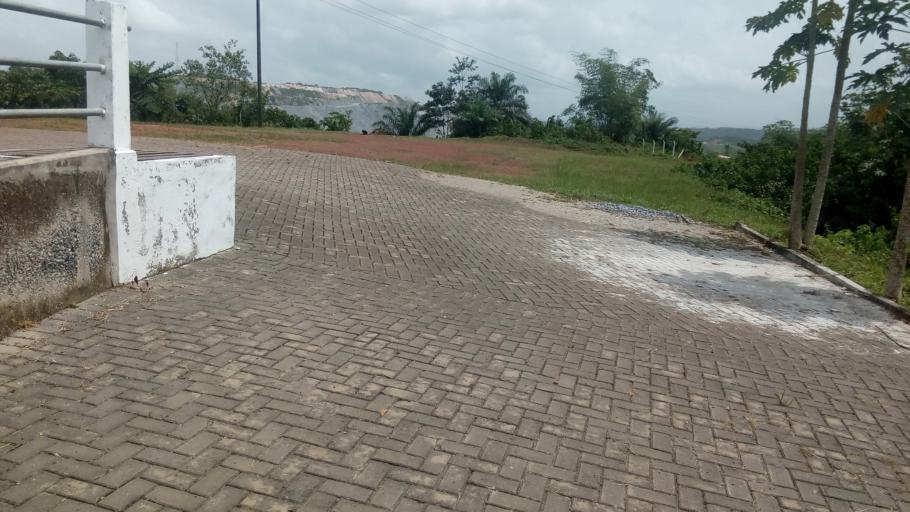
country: GH
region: Western
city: Tarkwa
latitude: 5.3011
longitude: -2.0100
